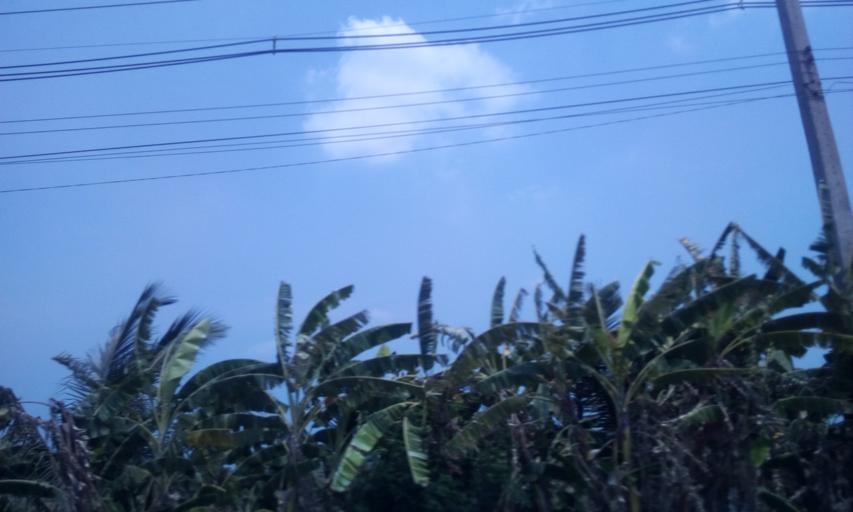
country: TH
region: Bangkok
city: Nong Chok
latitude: 13.9649
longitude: 100.9204
